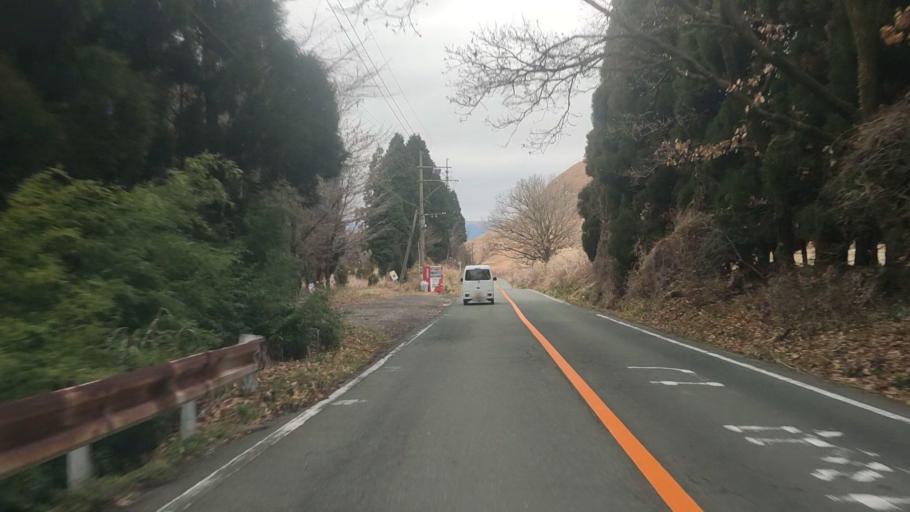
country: JP
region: Kumamoto
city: Aso
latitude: 32.9121
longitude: 131.1309
